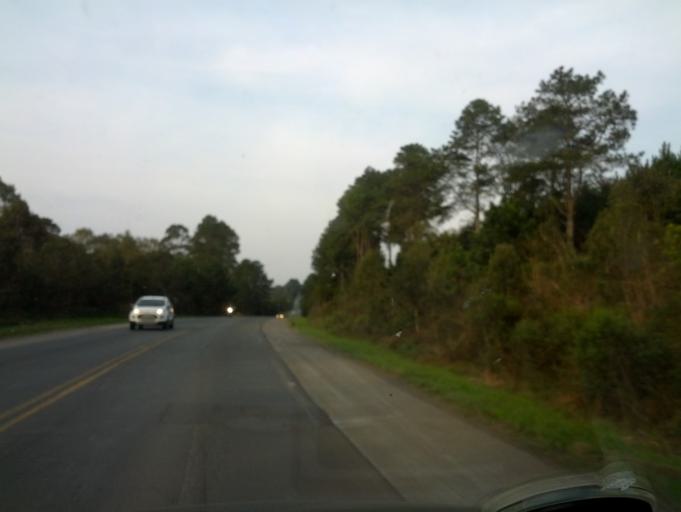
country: BR
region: Santa Catarina
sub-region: Otacilio Costa
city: Otacilio Costa
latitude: -27.3063
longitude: -50.1097
